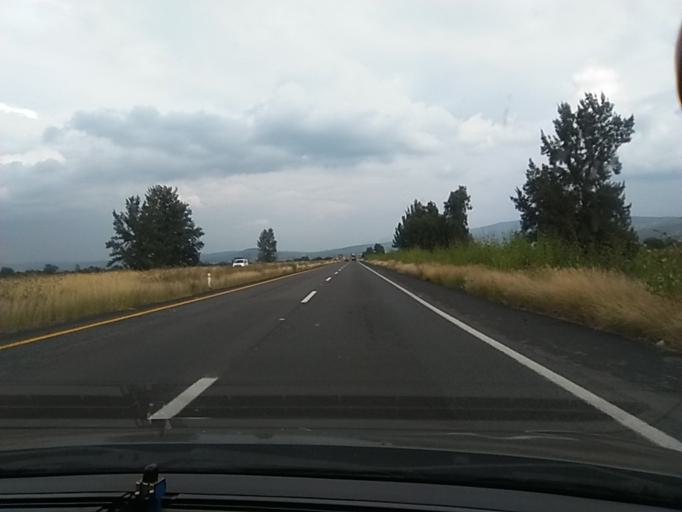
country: MX
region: Michoacan
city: Ecuandureo
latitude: 20.1774
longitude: -102.2539
